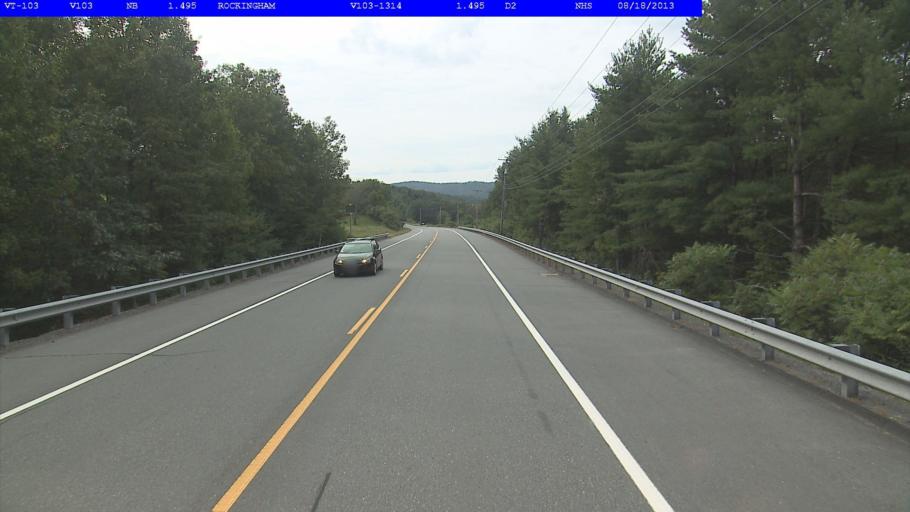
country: US
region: Vermont
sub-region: Windham County
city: Rockingham
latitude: 43.1887
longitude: -72.4842
